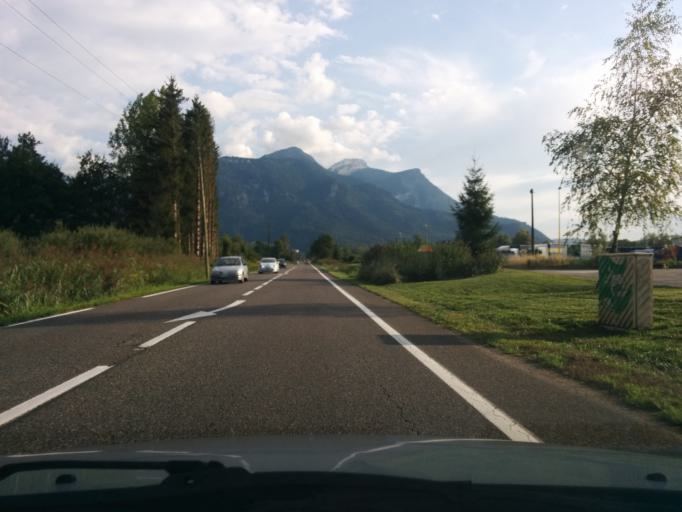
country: FR
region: Rhone-Alpes
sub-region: Departement de l'Isere
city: Entre-deux-Guiers
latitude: 45.4117
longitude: 5.7487
